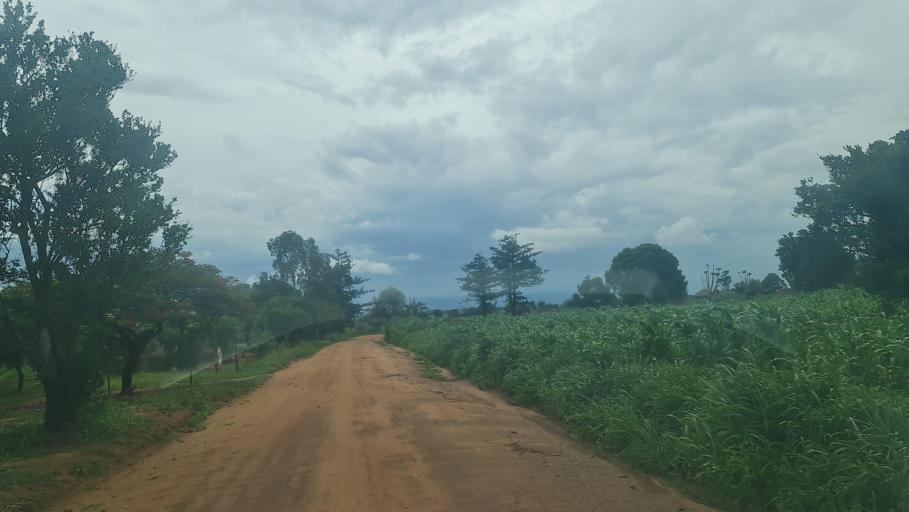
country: MW
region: Southern Region
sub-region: Nsanje District
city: Nsanje
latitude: -17.3950
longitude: 35.5727
